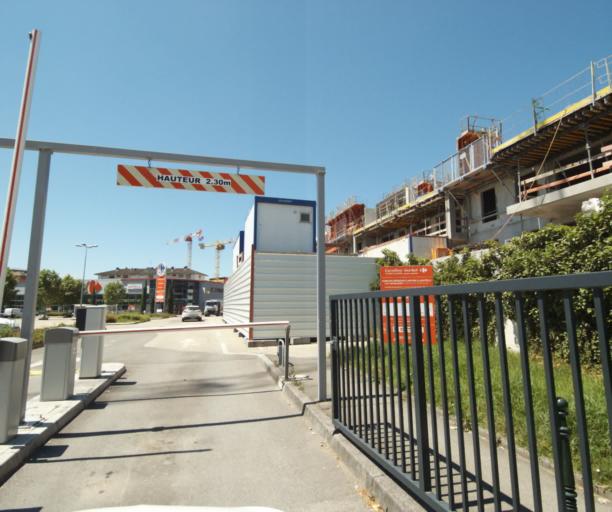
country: FR
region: Rhone-Alpes
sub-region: Departement de la Haute-Savoie
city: Thonon-les-Bains
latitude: 46.3725
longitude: 6.4857
